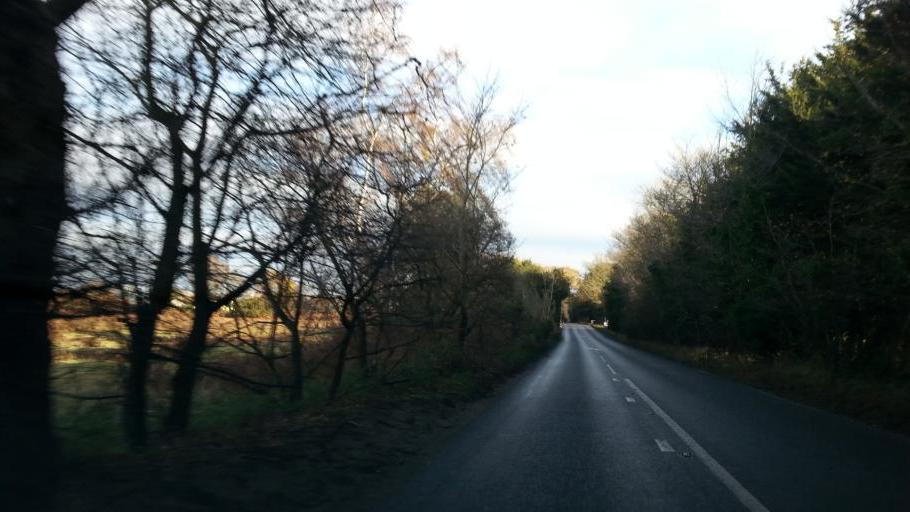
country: GB
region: England
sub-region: Suffolk
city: Woodbridge
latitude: 52.1044
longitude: 1.3671
